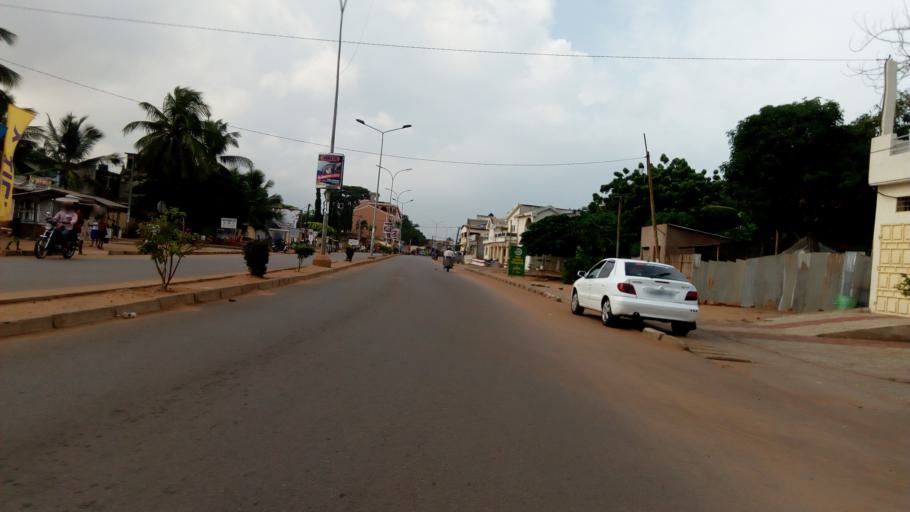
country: TG
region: Maritime
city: Lome
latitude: 6.2136
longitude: 1.2016
